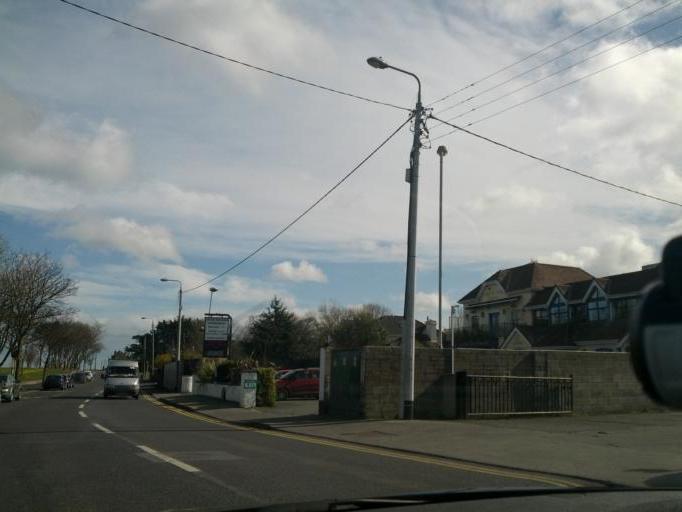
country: IE
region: Leinster
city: Malahide
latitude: 53.4502
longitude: -6.1416
